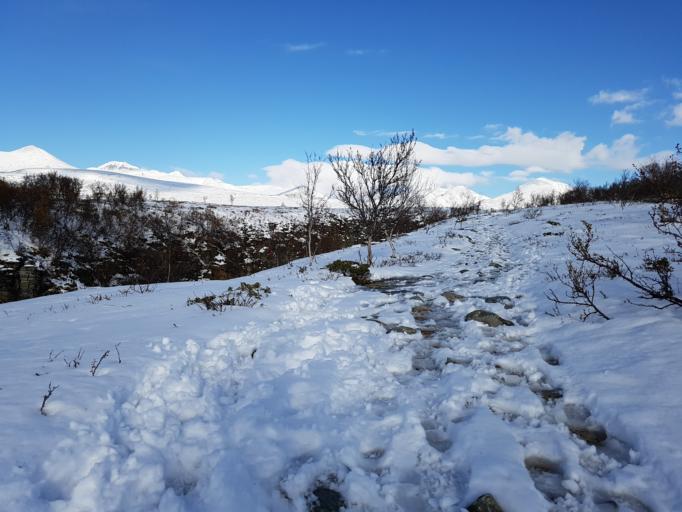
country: NO
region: Oppland
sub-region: Sel
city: Otta
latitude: 61.8292
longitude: 9.6973
